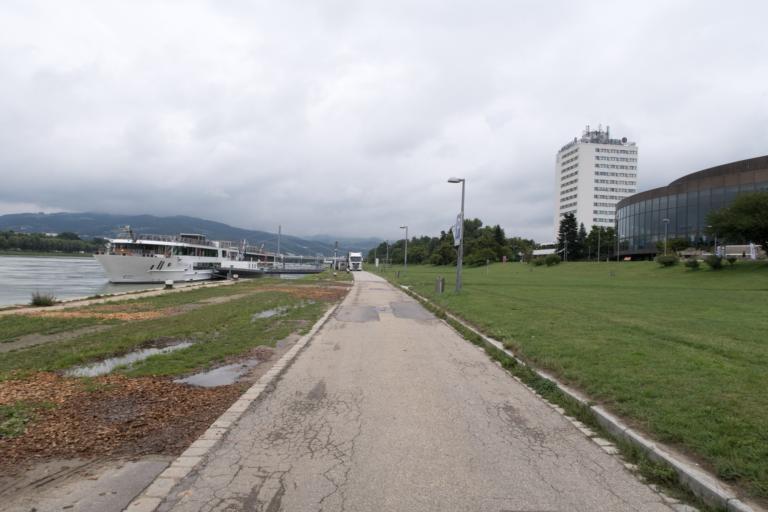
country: AT
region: Upper Austria
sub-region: Linz Stadt
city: Linz
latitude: 48.3104
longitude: 14.2912
